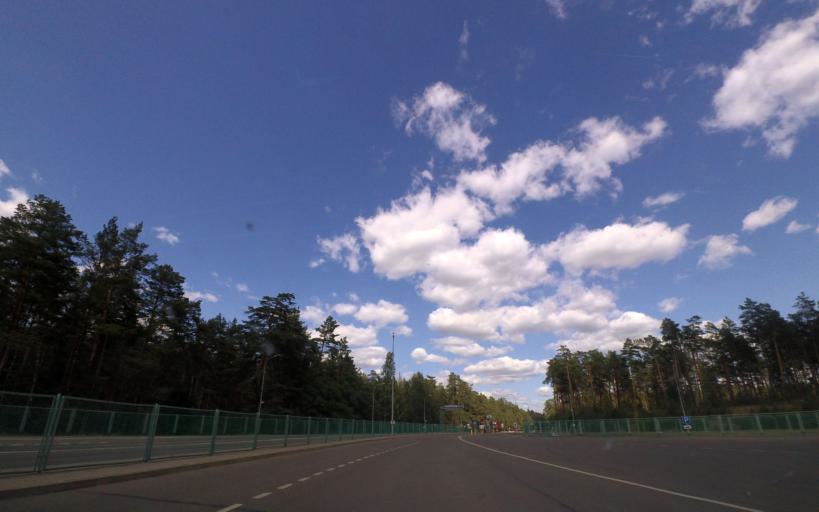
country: LT
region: Alytaus apskritis
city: Druskininkai
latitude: 53.9431
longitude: 23.9755
